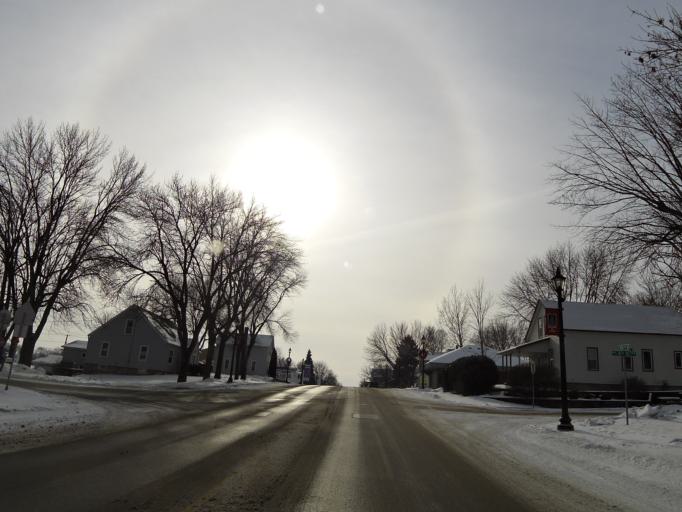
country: US
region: Minnesota
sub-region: Carver County
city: Mayer
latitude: 44.8883
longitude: -93.8880
